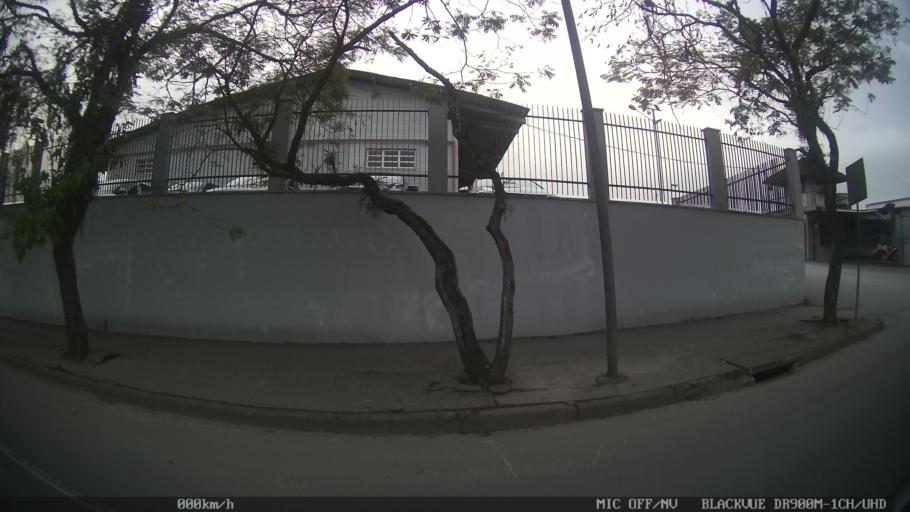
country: BR
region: Santa Catarina
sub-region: Joinville
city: Joinville
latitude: -26.2828
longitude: -48.8881
